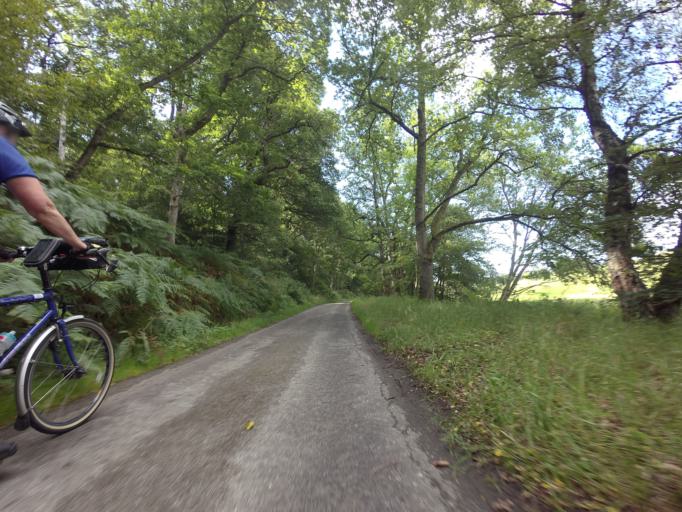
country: GB
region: Scotland
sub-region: Highland
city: Nairn
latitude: 57.5443
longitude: -3.8626
